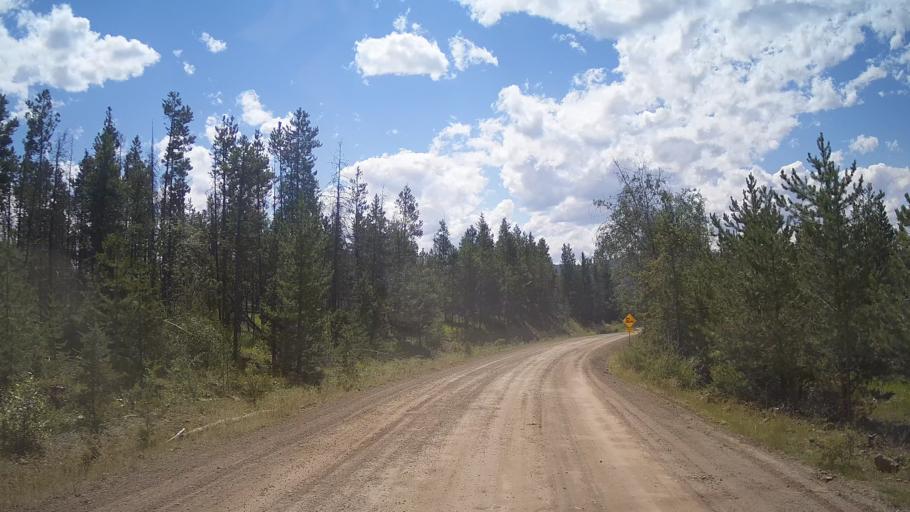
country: CA
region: British Columbia
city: Lillooet
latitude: 51.3382
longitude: -121.9550
